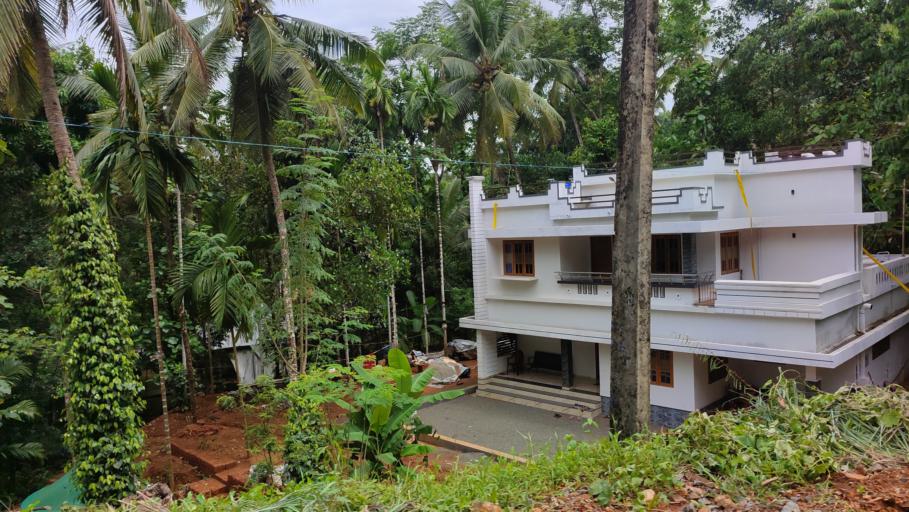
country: IN
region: Kerala
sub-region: Kasaragod District
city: Nileshwar
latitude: 12.2938
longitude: 75.2746
